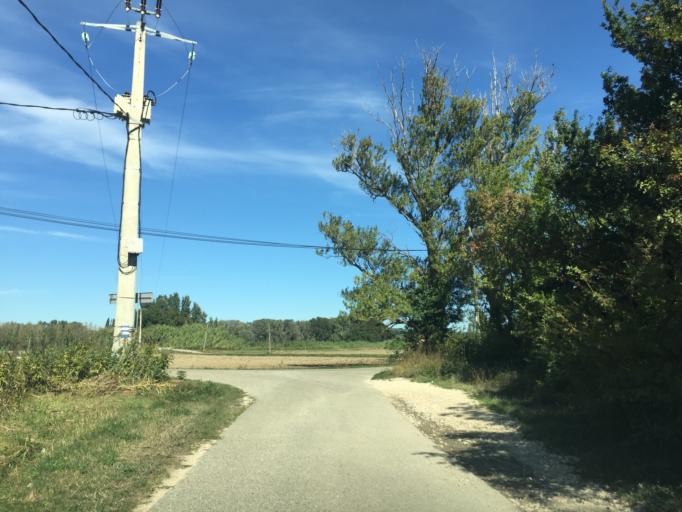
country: FR
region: Provence-Alpes-Cote d'Azur
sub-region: Departement du Vaucluse
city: Piolenc
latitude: 44.1651
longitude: 4.7368
